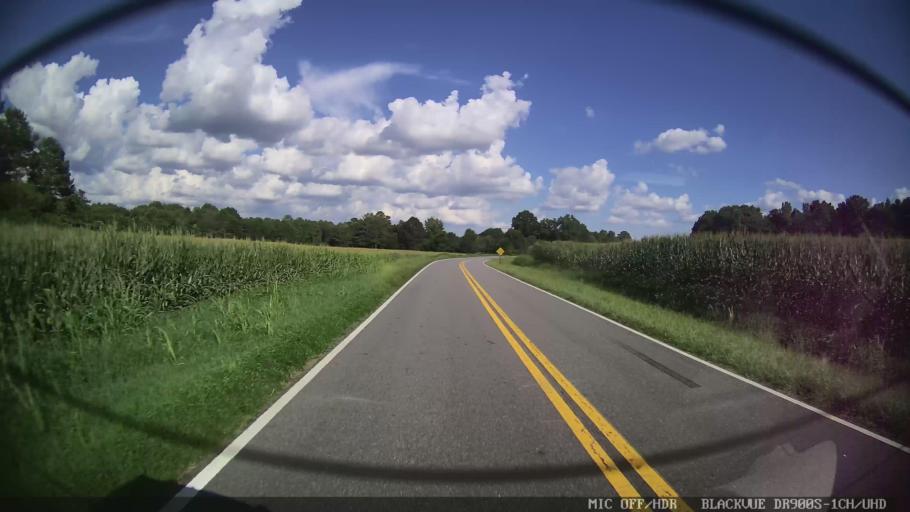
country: US
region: Georgia
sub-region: Bartow County
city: Euharlee
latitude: 34.1532
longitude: -84.9837
